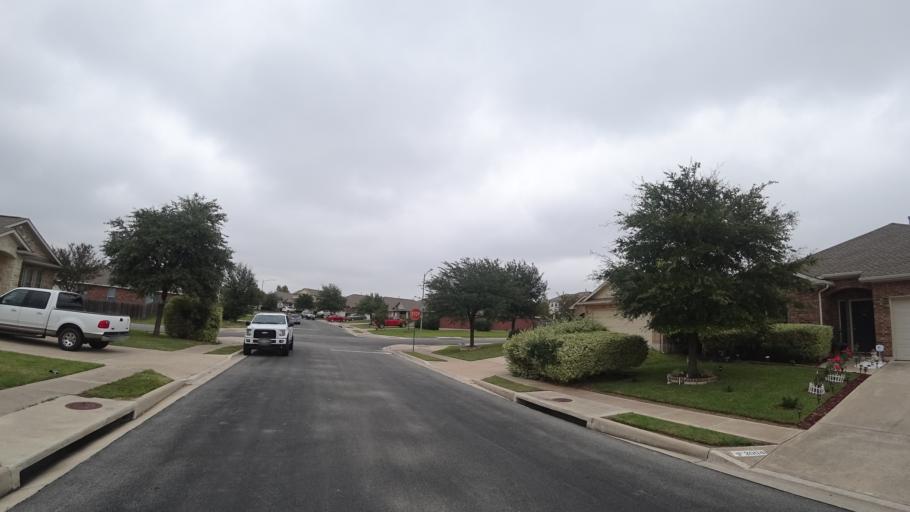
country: US
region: Texas
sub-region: Travis County
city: Pflugerville
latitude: 30.3750
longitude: -97.6516
